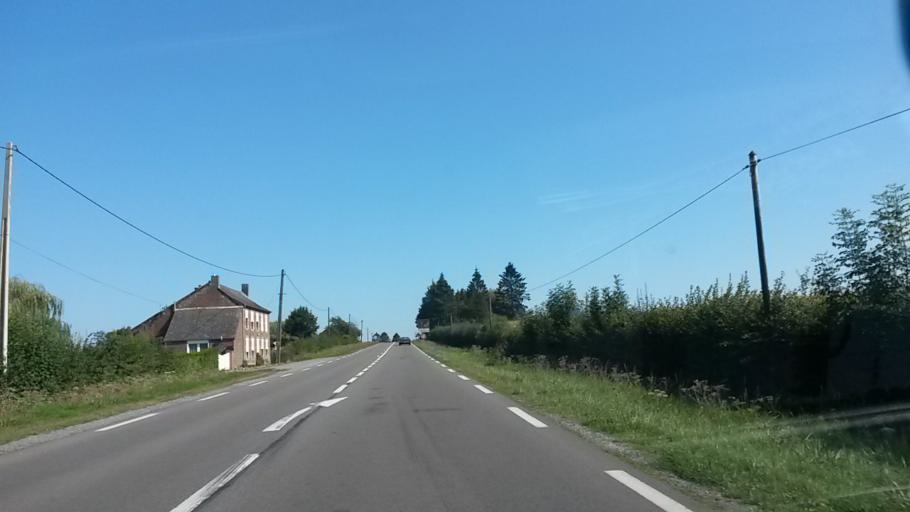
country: FR
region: Nord-Pas-de-Calais
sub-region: Departement du Nord
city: Avesnelles
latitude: 50.1506
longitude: 3.9521
